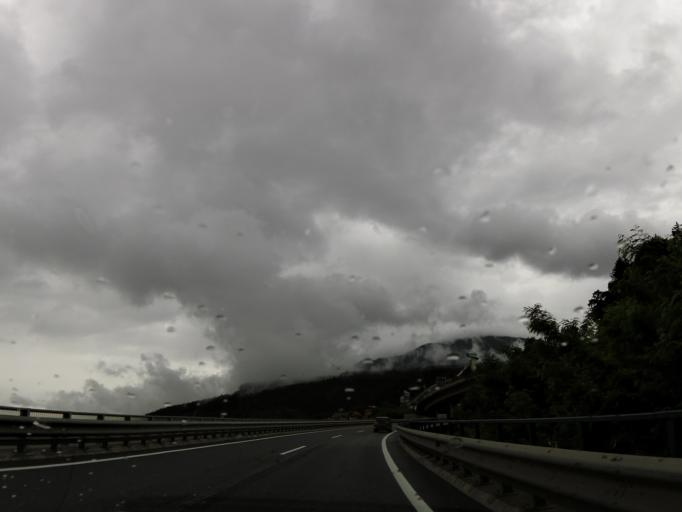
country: AT
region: Tyrol
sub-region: Innsbruck Stadt
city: Innsbruck
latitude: 47.2531
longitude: 11.3901
